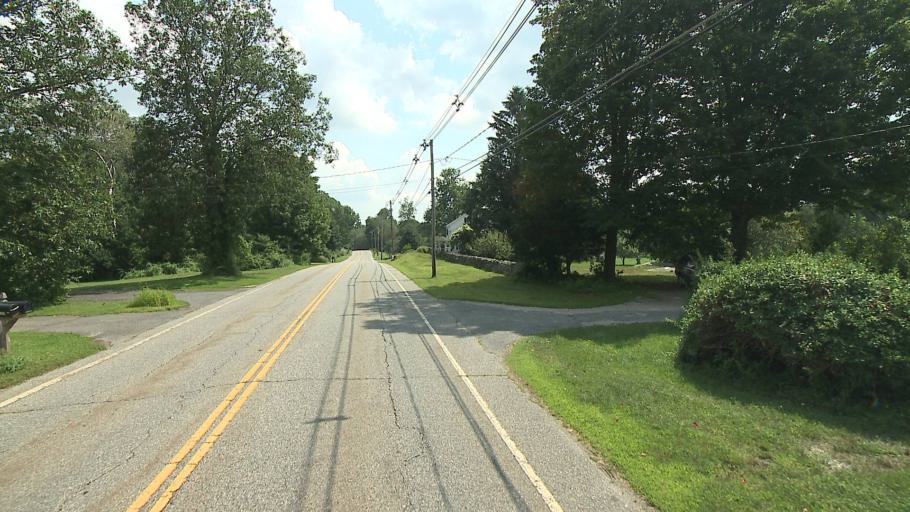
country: US
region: Connecticut
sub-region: Litchfield County
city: Bethlehem Village
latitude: 41.6853
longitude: -73.1713
